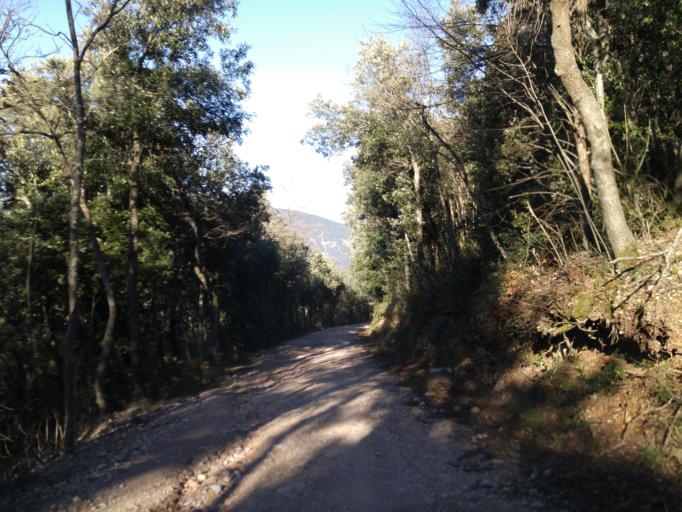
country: IT
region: The Marches
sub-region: Provincia di Pesaro e Urbino
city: Canavaccio
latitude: 43.6522
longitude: 12.7490
